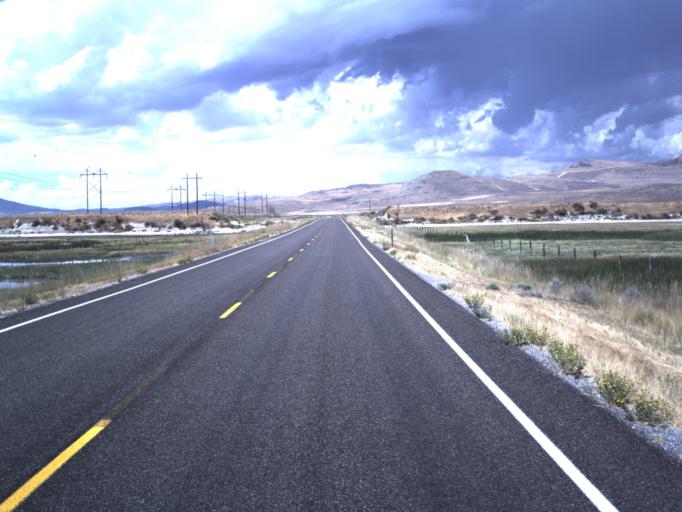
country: US
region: Utah
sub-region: Box Elder County
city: Tremonton
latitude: 41.6030
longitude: -112.3115
